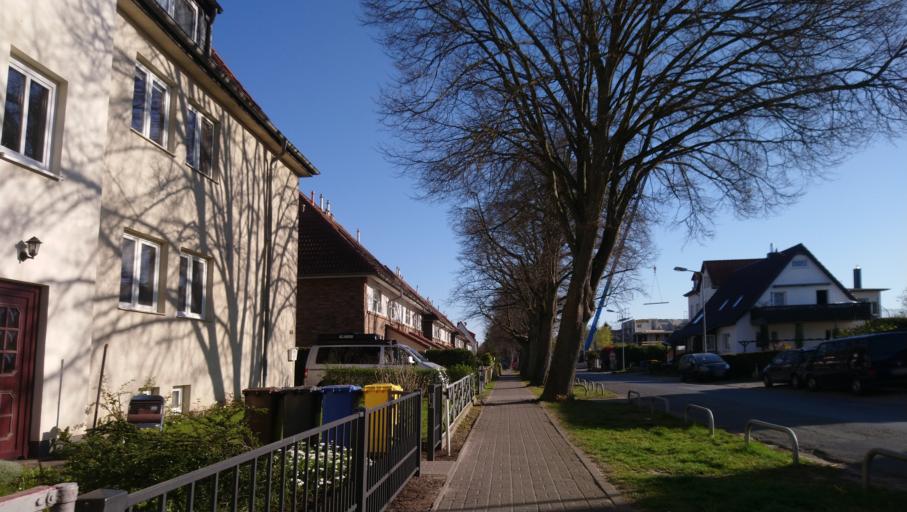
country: DE
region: Mecklenburg-Vorpommern
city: Rostock
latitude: 54.0678
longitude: 12.1338
